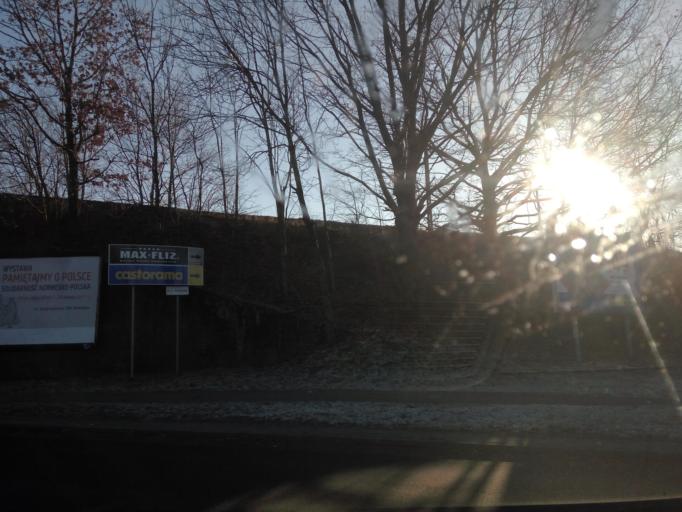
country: PL
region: Lower Silesian Voivodeship
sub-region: Powiat wroclawski
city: Smolec
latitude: 51.1211
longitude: 16.9462
